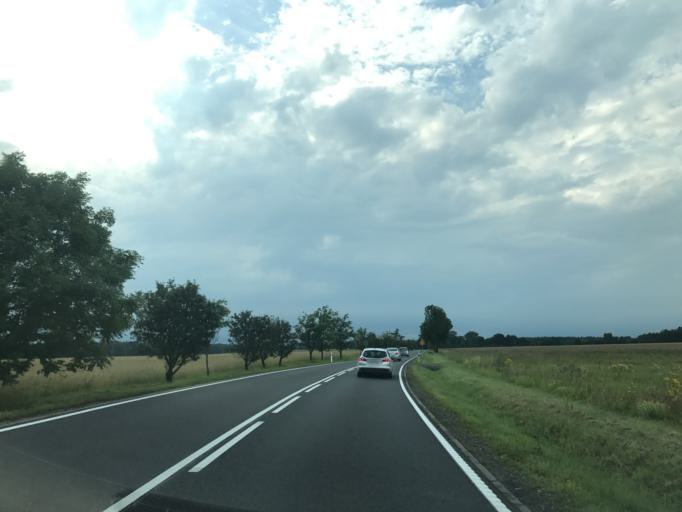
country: PL
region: Pomeranian Voivodeship
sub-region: Powiat czluchowski
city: Rzeczenica
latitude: 53.7422
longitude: 17.1787
